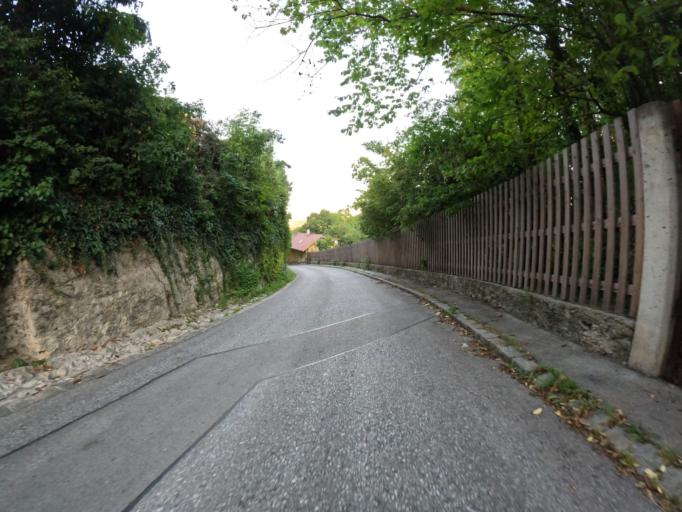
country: AT
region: Lower Austria
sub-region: Politischer Bezirk Baden
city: Baden
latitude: 48.0115
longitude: 16.2191
